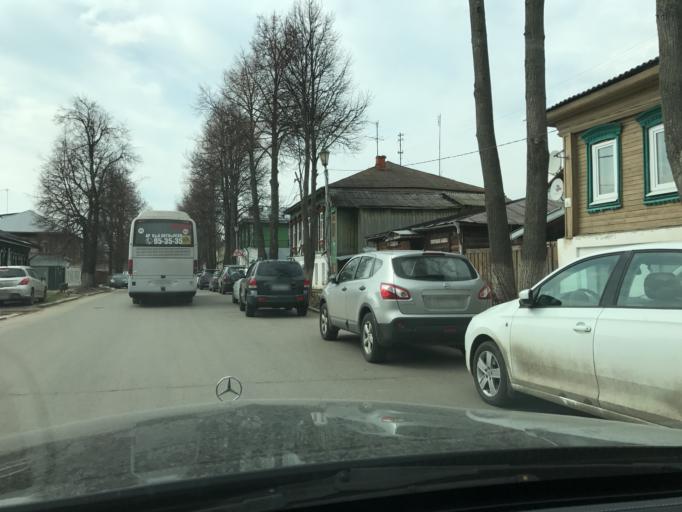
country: RU
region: Vladimir
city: Suzdal'
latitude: 56.4199
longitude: 40.4553
